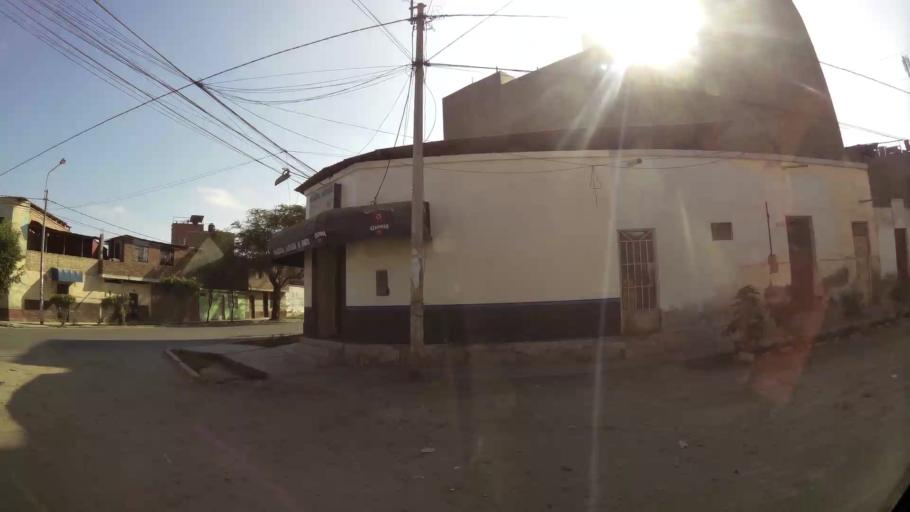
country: PE
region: Lambayeque
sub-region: Provincia de Chiclayo
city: Chiclayo
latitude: -6.7674
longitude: -79.8465
